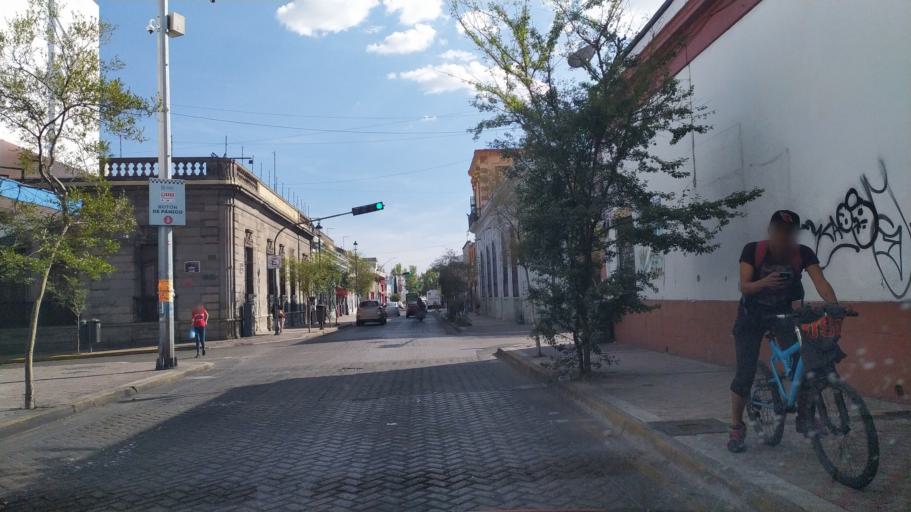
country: MX
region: Jalisco
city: Guadalajara
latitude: 20.6737
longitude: -103.3524
